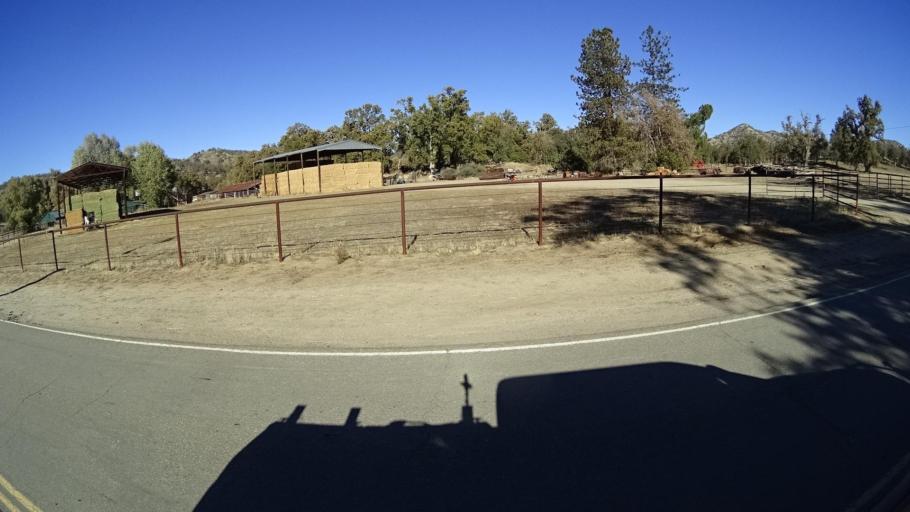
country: US
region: California
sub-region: Kern County
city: Alta Sierra
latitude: 35.7715
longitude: -118.7092
